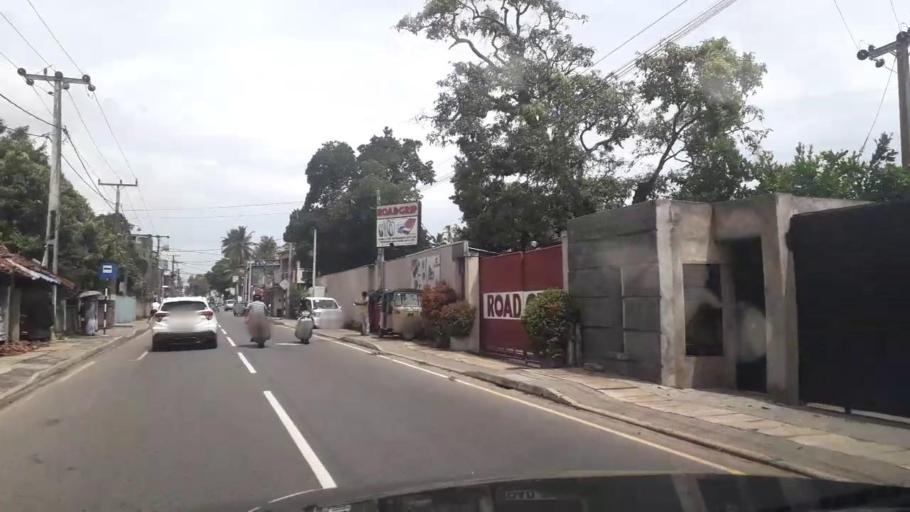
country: LK
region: Western
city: Moratuwa
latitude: 6.7550
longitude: 79.8991
